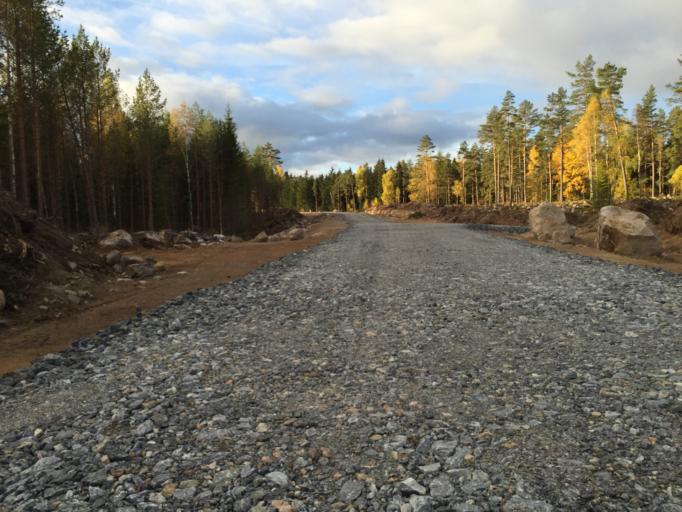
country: SE
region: Vaestmanland
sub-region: Hallstahammars Kommun
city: Hallstahammar
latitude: 59.6350
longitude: 16.2000
